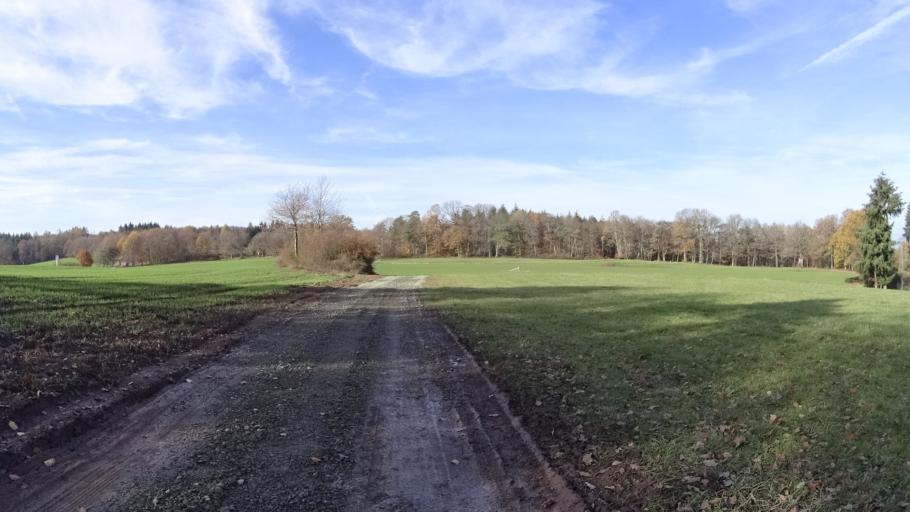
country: DE
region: Rheinland-Pfalz
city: Kirrweiler
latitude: 49.6493
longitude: 7.4913
